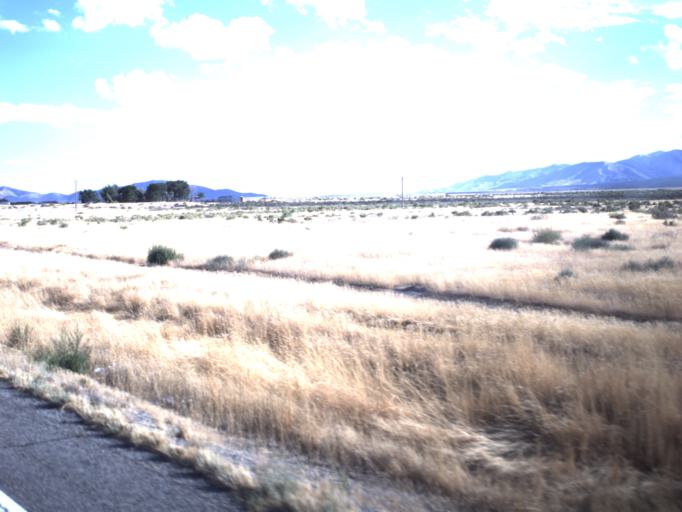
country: US
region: Utah
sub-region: Tooele County
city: Grantsville
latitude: 40.6094
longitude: -112.4918
